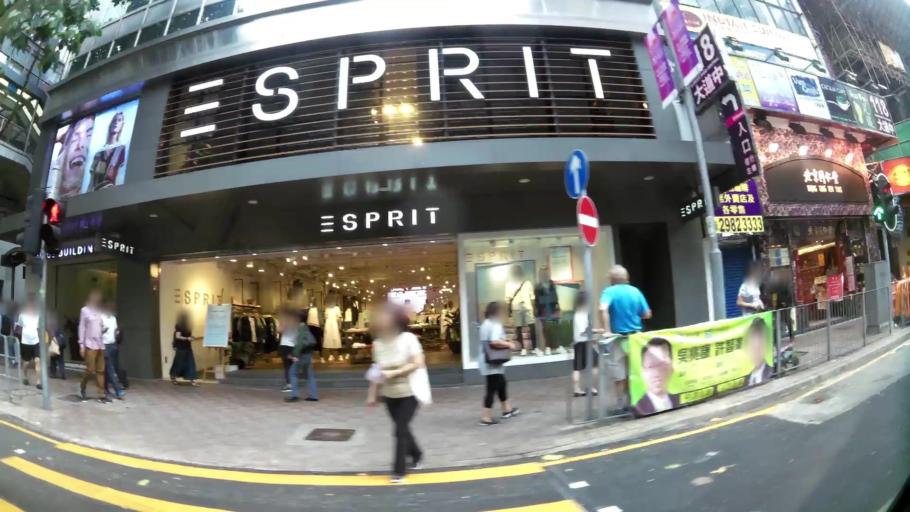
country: HK
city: Hong Kong
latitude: 22.2836
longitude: 114.1547
